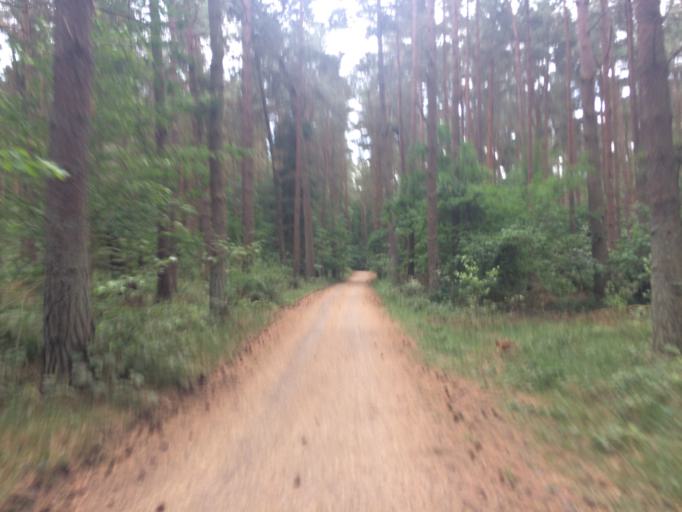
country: DK
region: Capital Region
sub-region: Bornholm Kommune
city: Ronne
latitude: 55.1401
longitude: 14.7160
